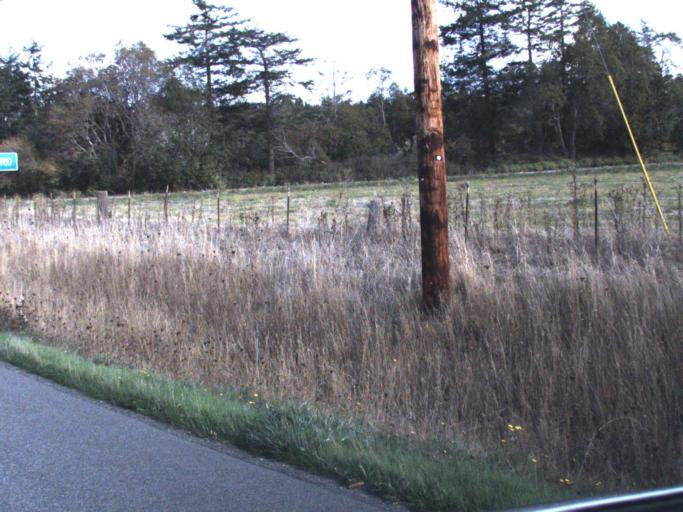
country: US
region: Washington
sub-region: Island County
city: Coupeville
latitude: 48.2600
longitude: -122.6982
